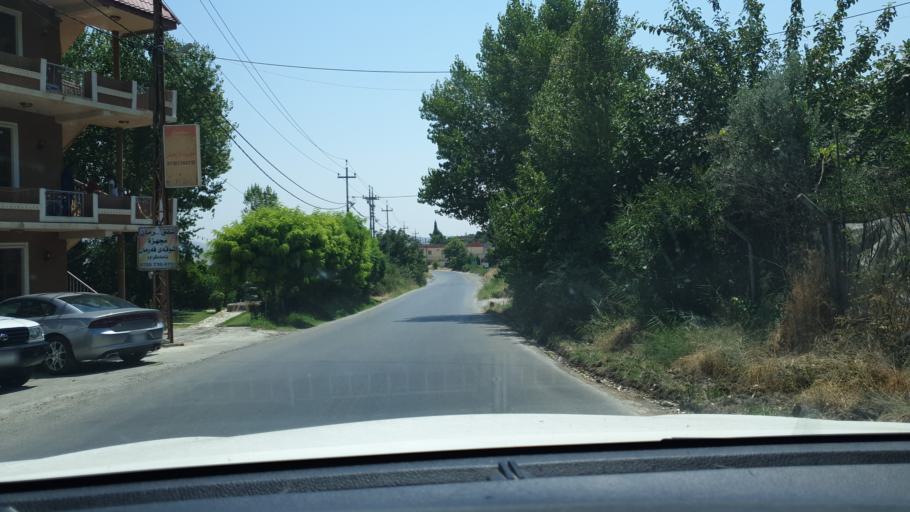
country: IQ
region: Arbil
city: Nahiyat Hiran
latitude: 36.2903
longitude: 44.4816
